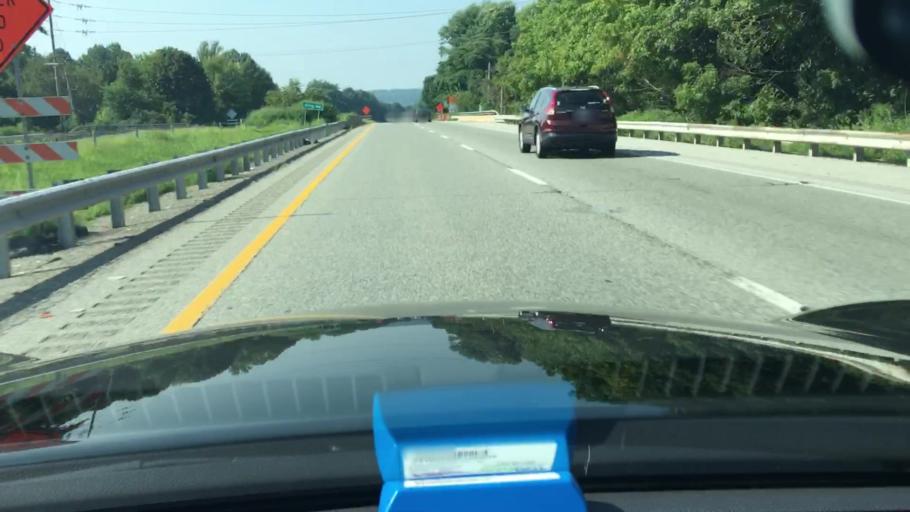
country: US
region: Pennsylvania
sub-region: Chester County
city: Exton
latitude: 40.0186
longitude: -75.5855
